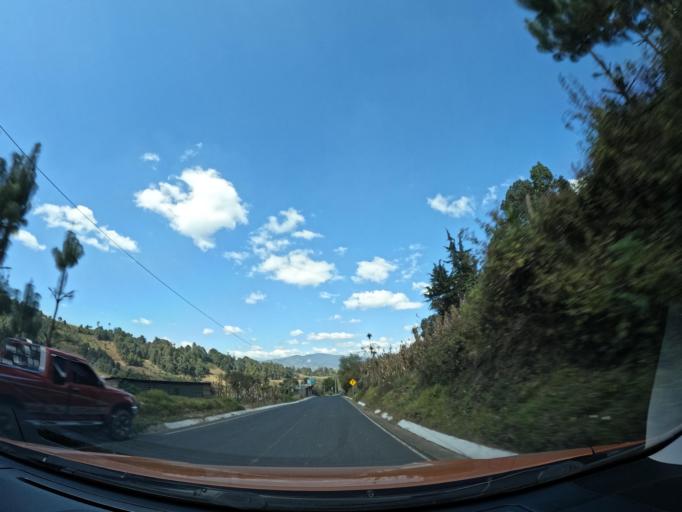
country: GT
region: Chimaltenango
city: Patzun
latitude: 14.6578
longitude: -91.0196
